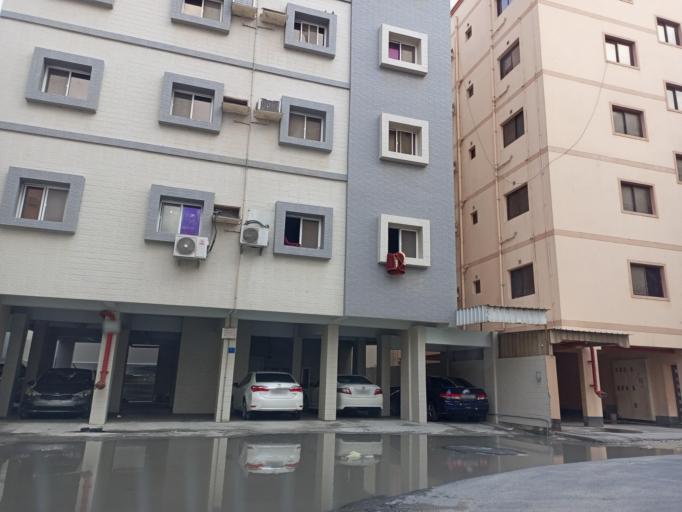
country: BH
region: Muharraq
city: Al Hadd
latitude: 26.2416
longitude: 50.6467
